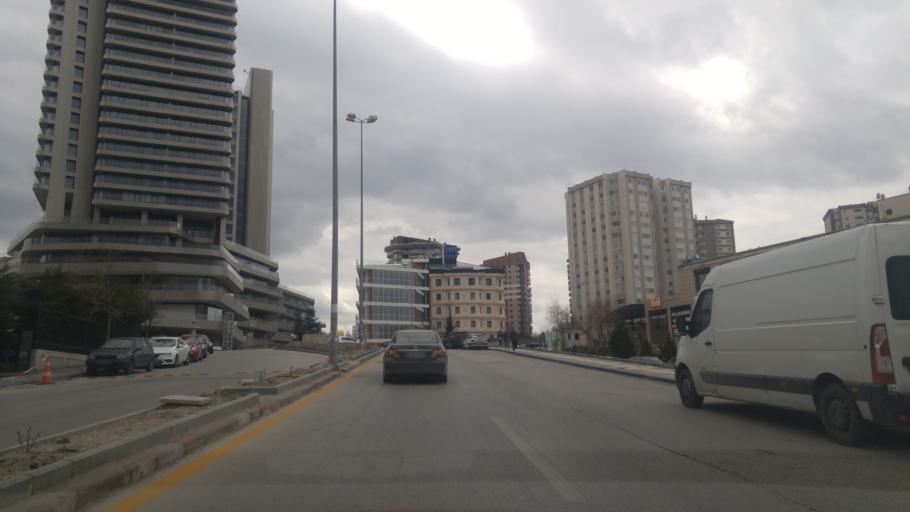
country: TR
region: Ankara
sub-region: Goelbasi
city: Golbasi
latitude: 39.8475
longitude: 32.8295
